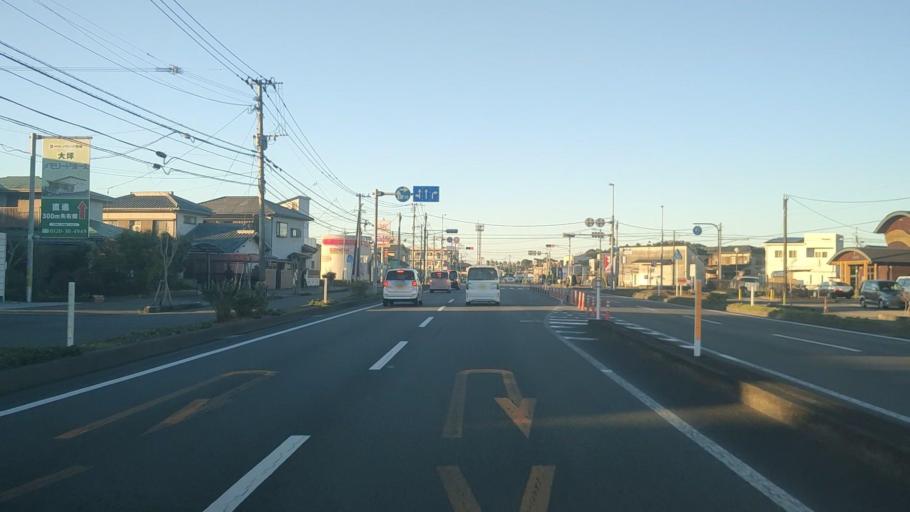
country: JP
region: Miyazaki
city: Miyazaki-shi
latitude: 31.8977
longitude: 131.4063
